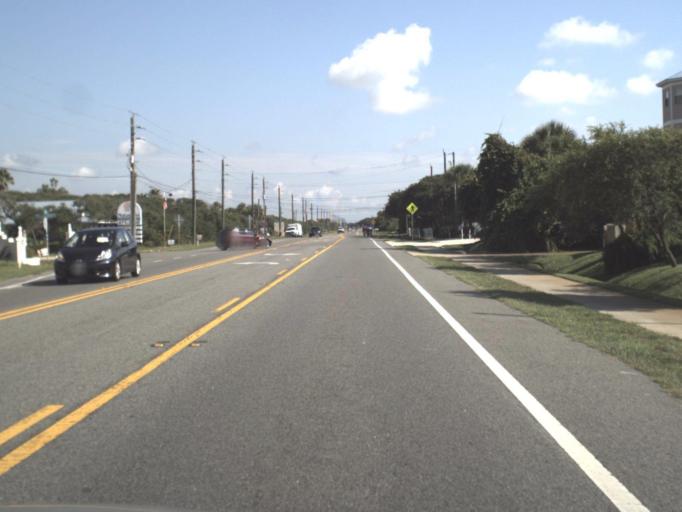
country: US
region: Florida
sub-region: Saint Johns County
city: Butler Beach
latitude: 29.7817
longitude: -81.2579
